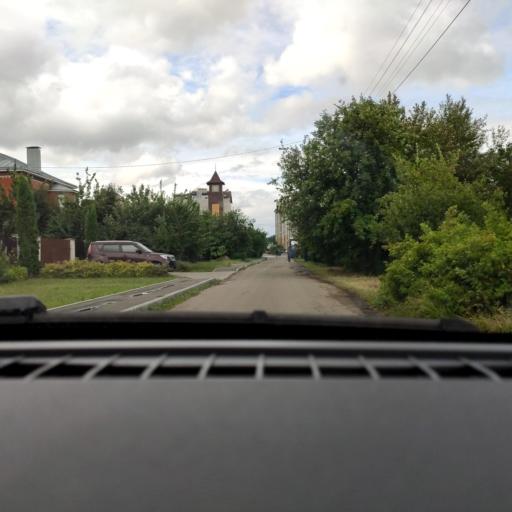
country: RU
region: Voronezj
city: Novaya Usman'
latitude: 51.6485
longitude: 39.3326
